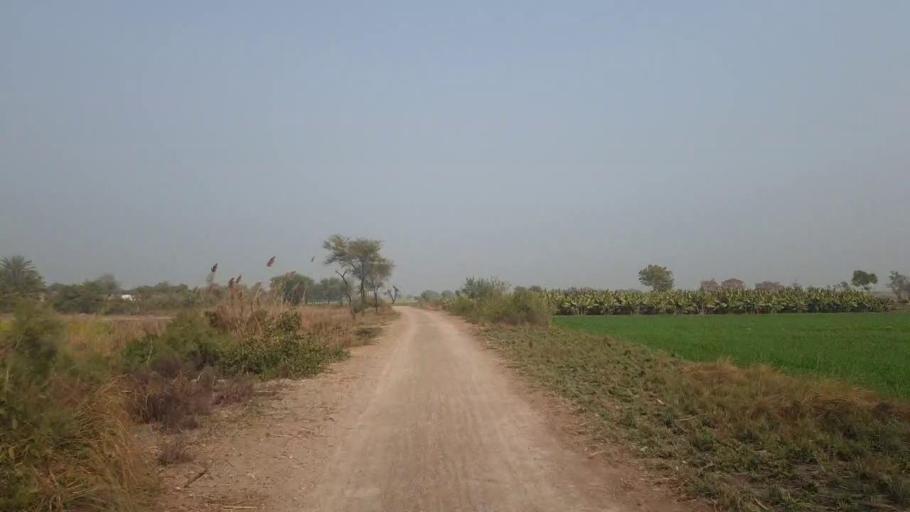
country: PK
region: Sindh
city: Tando Adam
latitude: 25.8315
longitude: 68.5991
